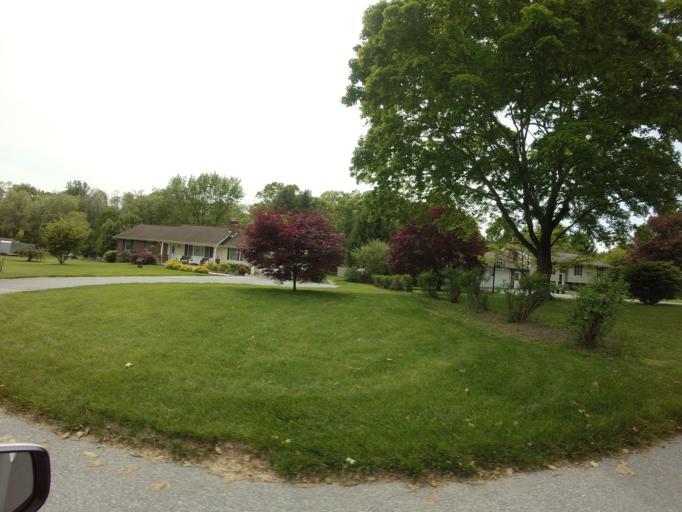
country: US
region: Maryland
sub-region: Carroll County
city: Eldersburg
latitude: 39.4622
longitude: -76.9597
